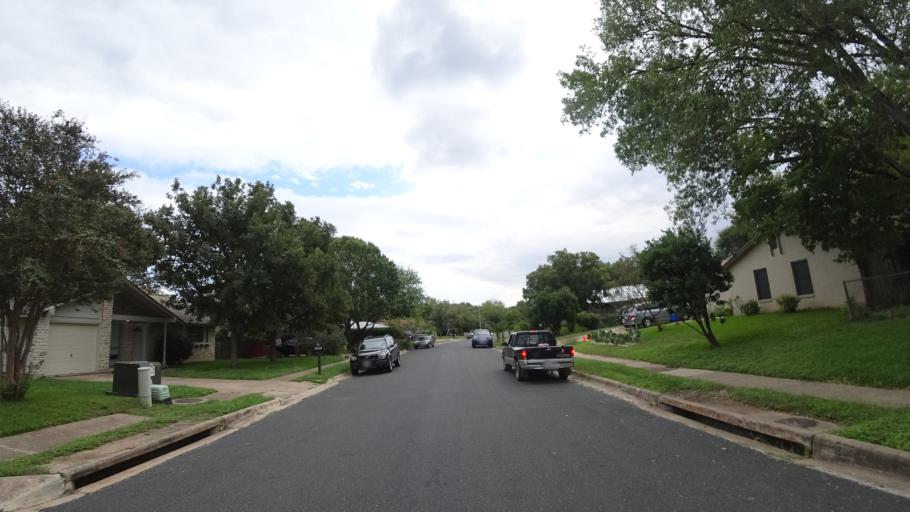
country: US
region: Texas
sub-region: Travis County
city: Rollingwood
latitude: 30.2152
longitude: -97.7801
